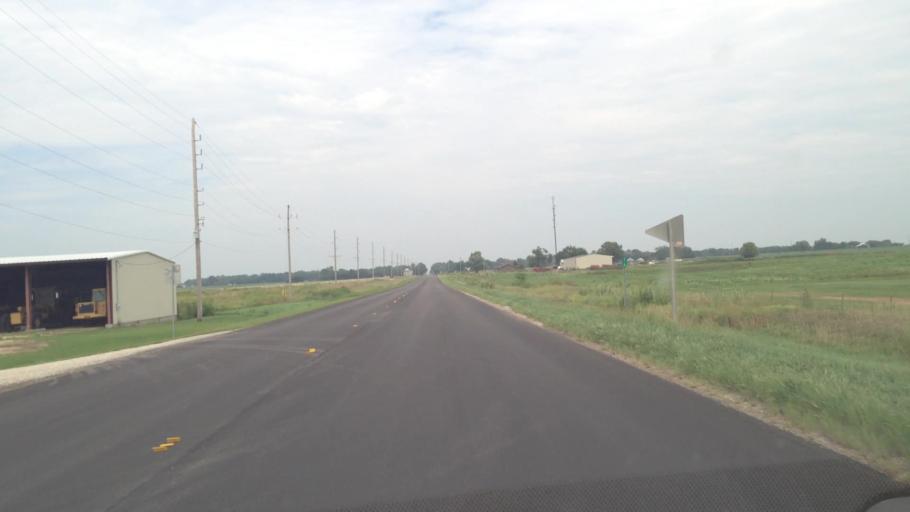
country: US
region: Kansas
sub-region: Allen County
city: Iola
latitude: 37.8963
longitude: -95.1705
